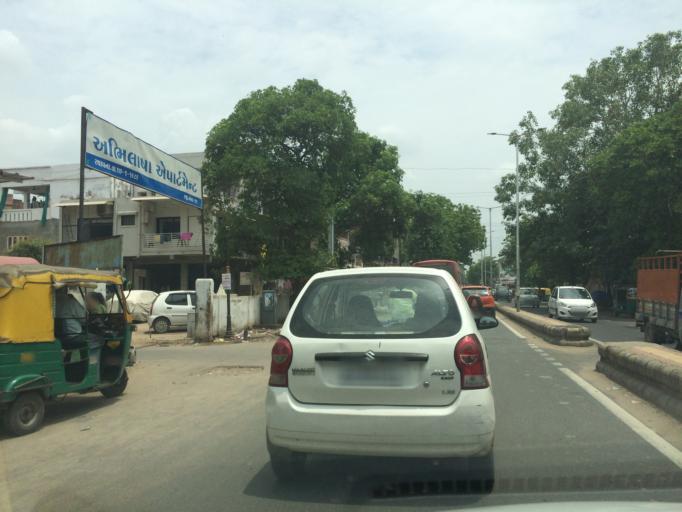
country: IN
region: Gujarat
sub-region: Ahmadabad
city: Ahmedabad
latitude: 23.0690
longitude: 72.5663
